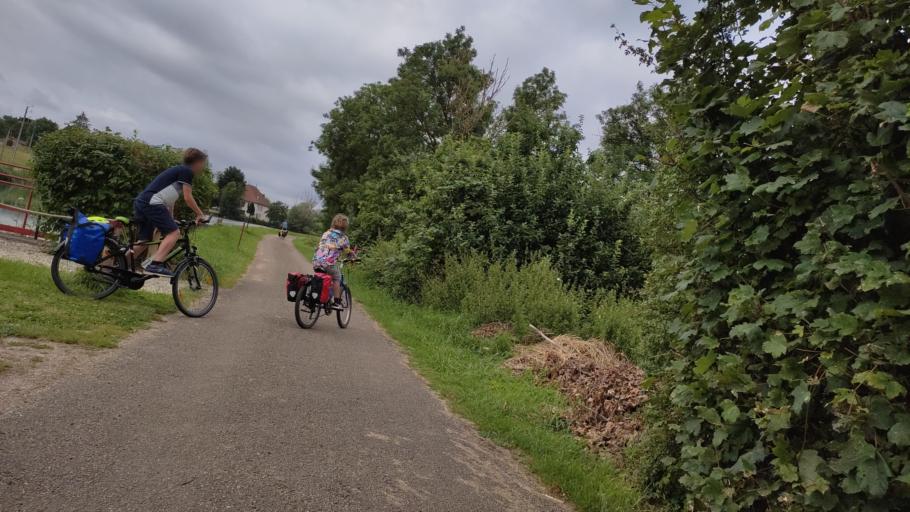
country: FR
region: Bourgogne
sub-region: Departement de l'Yonne
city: Tanlay
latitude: 47.7967
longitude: 4.0913
